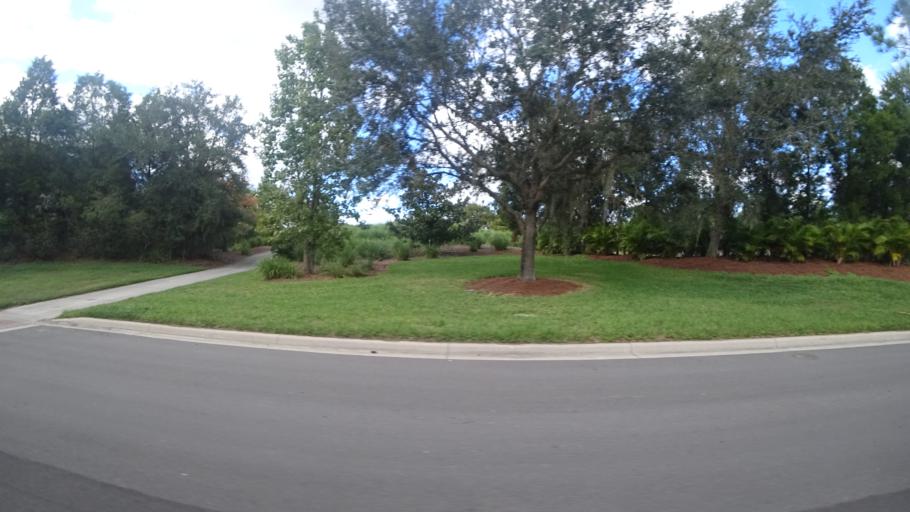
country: US
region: Florida
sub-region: Sarasota County
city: The Meadows
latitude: 27.4139
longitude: -82.4144
